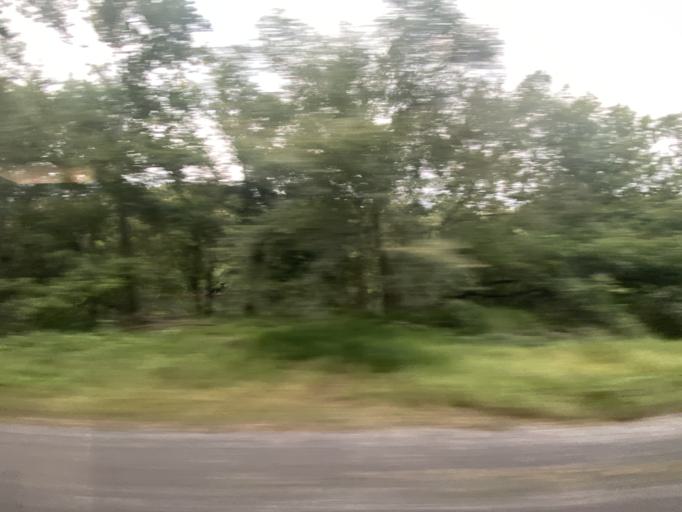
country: US
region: West Virginia
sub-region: Mineral County
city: Fort Ashby
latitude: 39.5298
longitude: -78.5905
